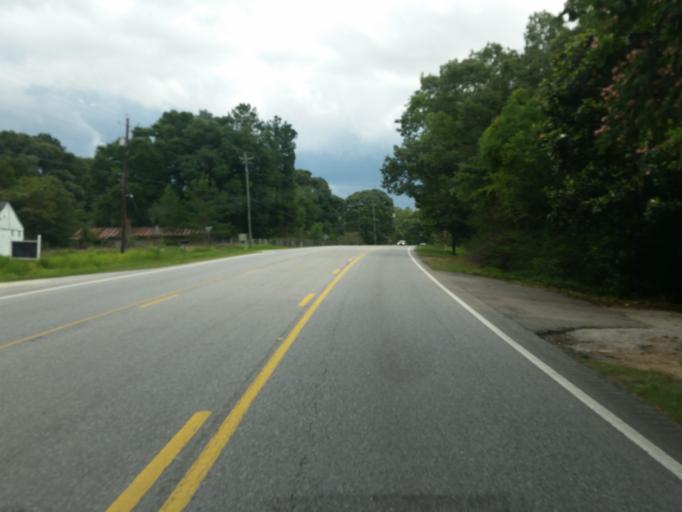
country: US
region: Mississippi
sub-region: George County
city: Lucedale
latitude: 30.8482
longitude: -88.3974
